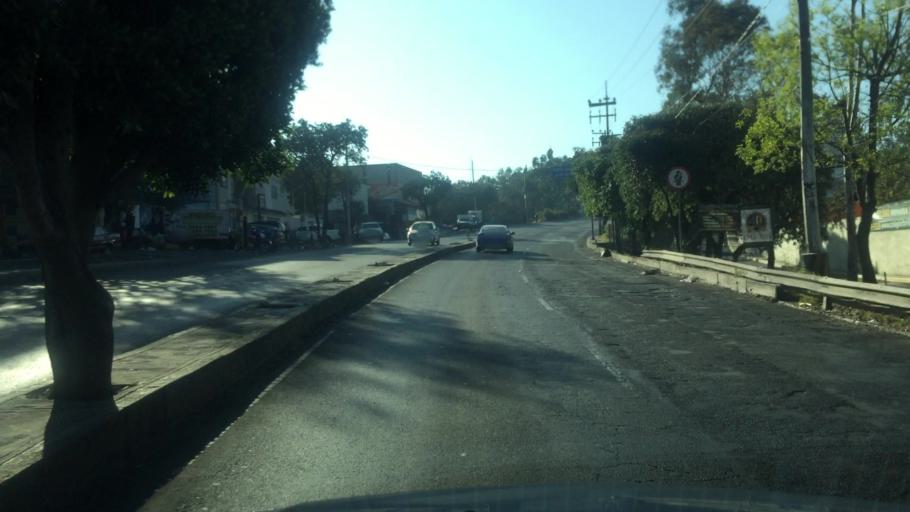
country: MX
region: Mexico City
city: Tlalpan
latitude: 19.2734
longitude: -99.2065
